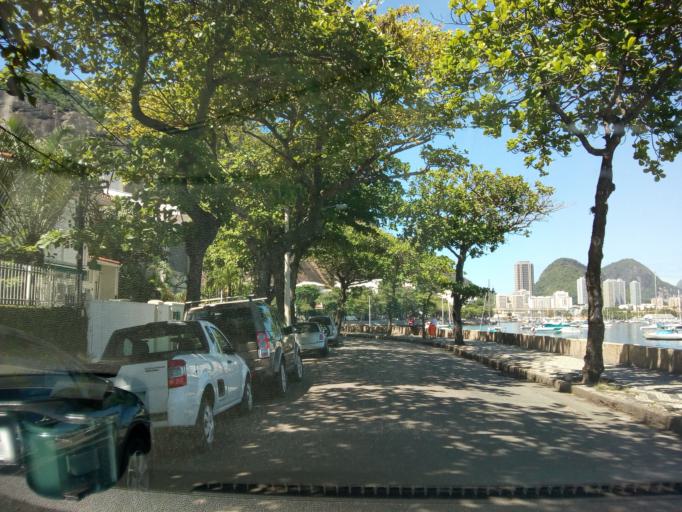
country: BR
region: Rio de Janeiro
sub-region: Rio De Janeiro
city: Rio de Janeiro
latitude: -22.9454
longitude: -43.1634
